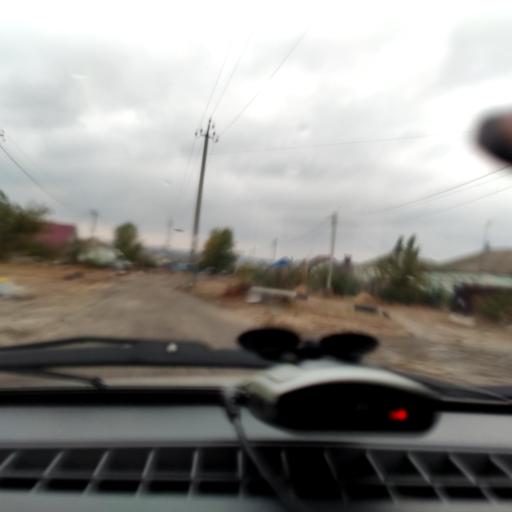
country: RU
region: Voronezj
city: Pridonskoy
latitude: 51.7029
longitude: 39.0702
